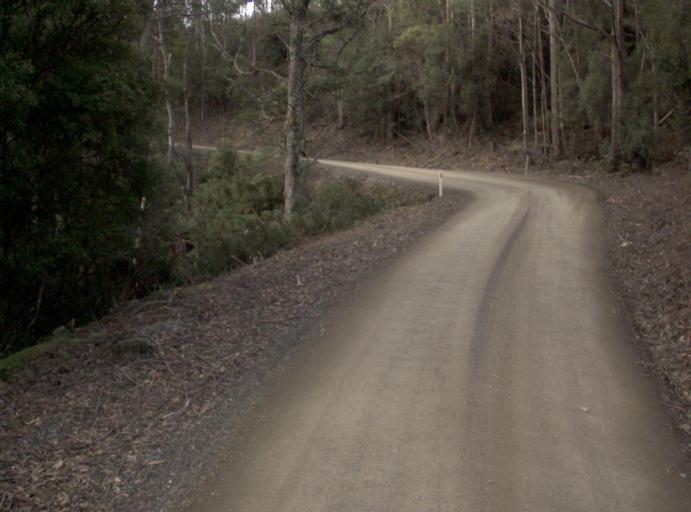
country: AU
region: Tasmania
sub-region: Dorset
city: Scottsdale
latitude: -41.2829
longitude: 147.3390
